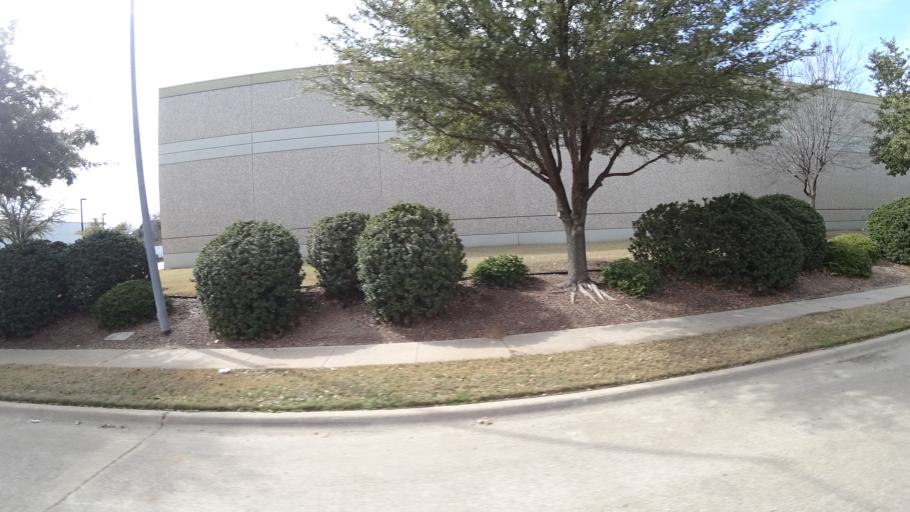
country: US
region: Texas
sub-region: Denton County
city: Lewisville
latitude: 33.0262
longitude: -96.9789
